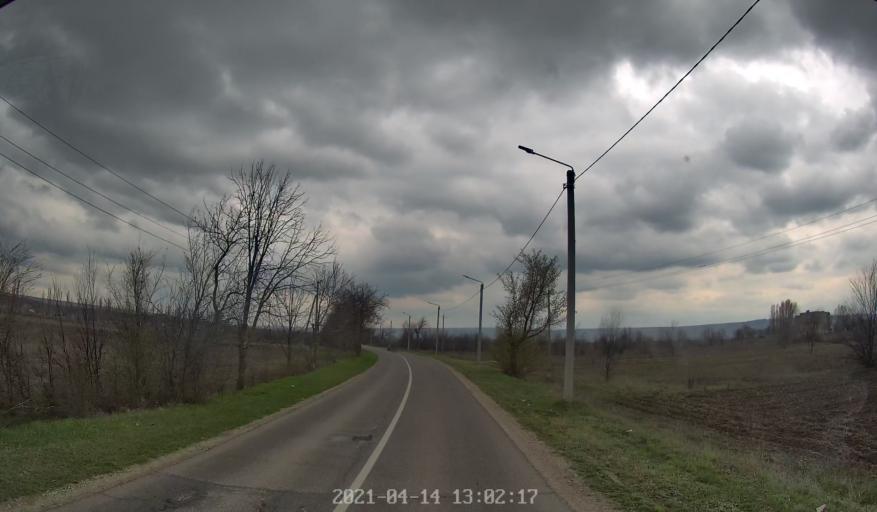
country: MD
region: Chisinau
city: Vadul lui Voda
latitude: 47.1247
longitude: 29.1112
